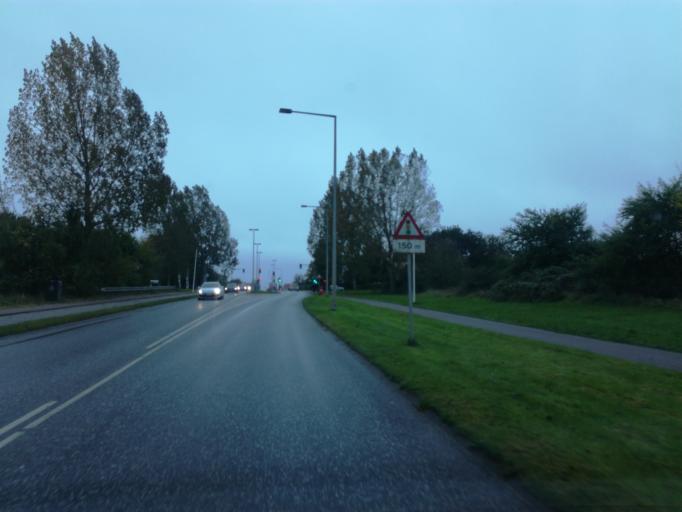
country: DK
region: South Denmark
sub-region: Fredericia Kommune
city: Fredericia
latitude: 55.5736
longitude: 9.7252
